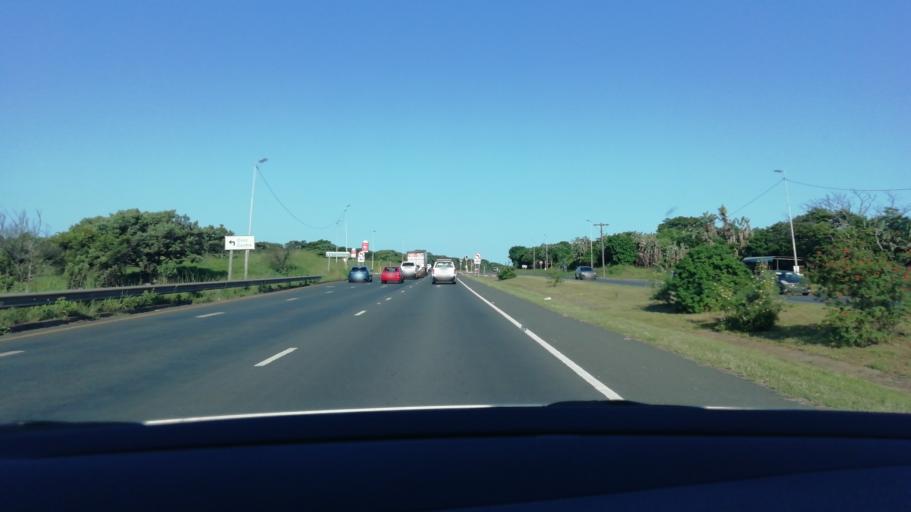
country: ZA
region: KwaZulu-Natal
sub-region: uThungulu District Municipality
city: Richards Bay
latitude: -28.7683
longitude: 32.0473
